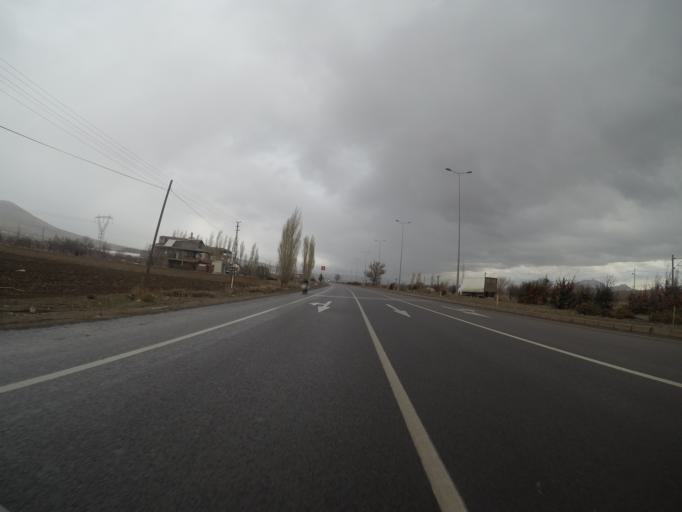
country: TR
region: Kayseri
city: Incesu
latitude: 38.6981
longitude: 35.2500
